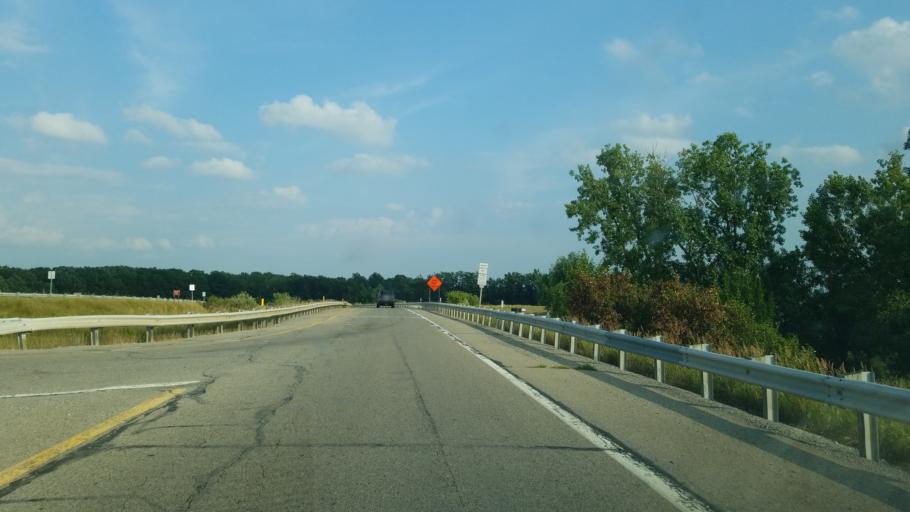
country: US
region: Michigan
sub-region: Gratiot County
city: Alma
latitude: 43.4075
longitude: -84.6637
